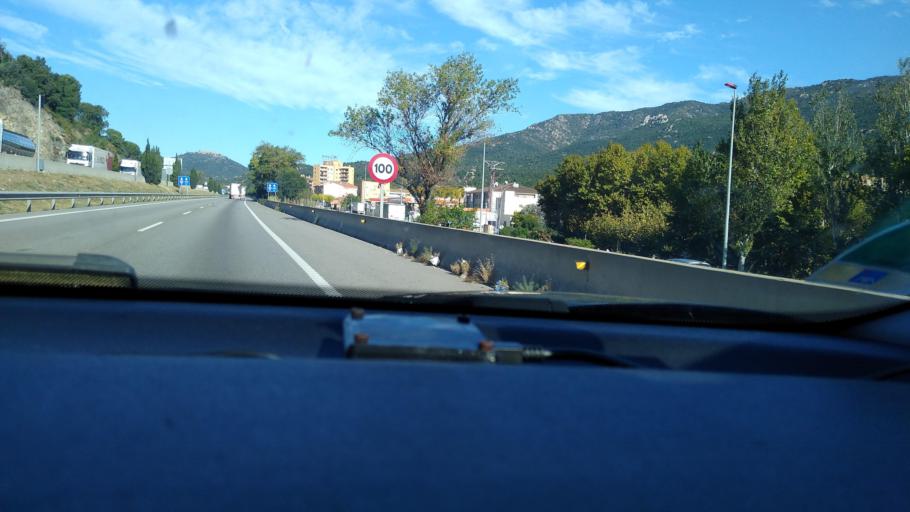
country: ES
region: Catalonia
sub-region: Provincia de Girona
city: la Jonquera
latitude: 42.4153
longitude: 2.8718
